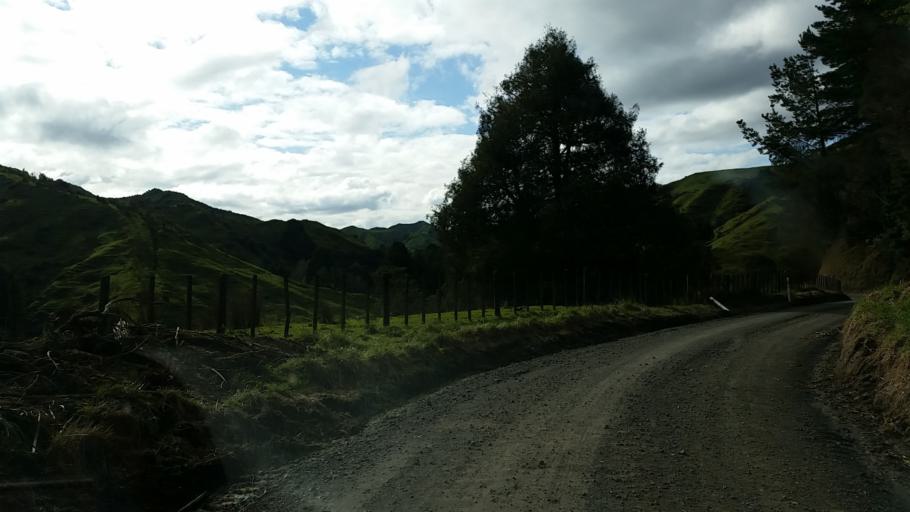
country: NZ
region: Taranaki
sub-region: New Plymouth District
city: Waitara
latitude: -39.1554
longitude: 174.5584
